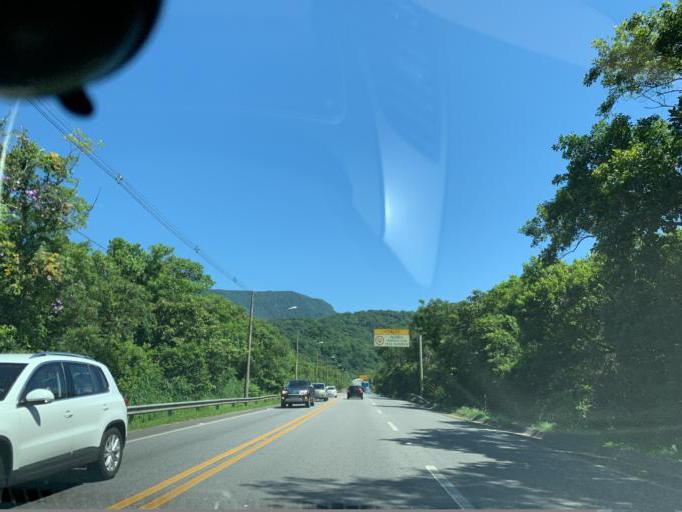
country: BR
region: Sao Paulo
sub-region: Bertioga
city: Bertioga
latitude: -23.7611
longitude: -46.0378
